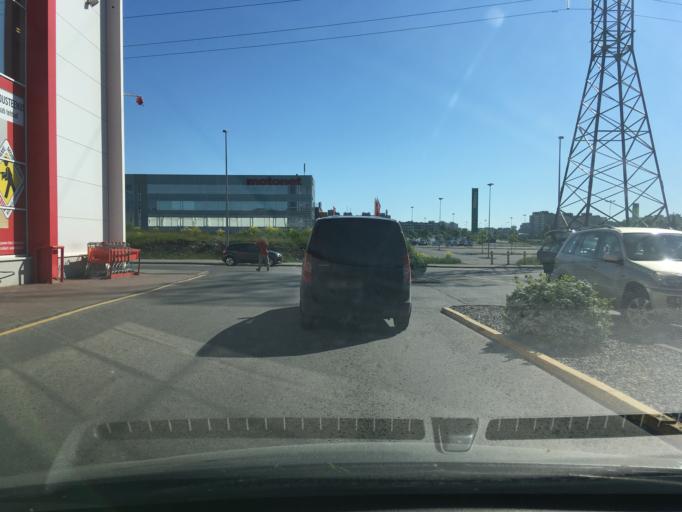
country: EE
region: Harju
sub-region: Tallinna linn
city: Kose
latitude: 59.4420
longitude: 24.8586
